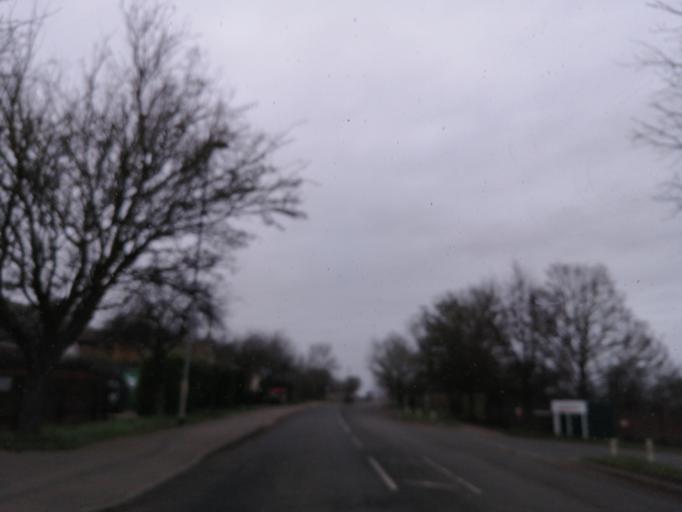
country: GB
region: England
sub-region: Cambridgeshire
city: Yaxley
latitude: 52.5232
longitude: -0.2435
